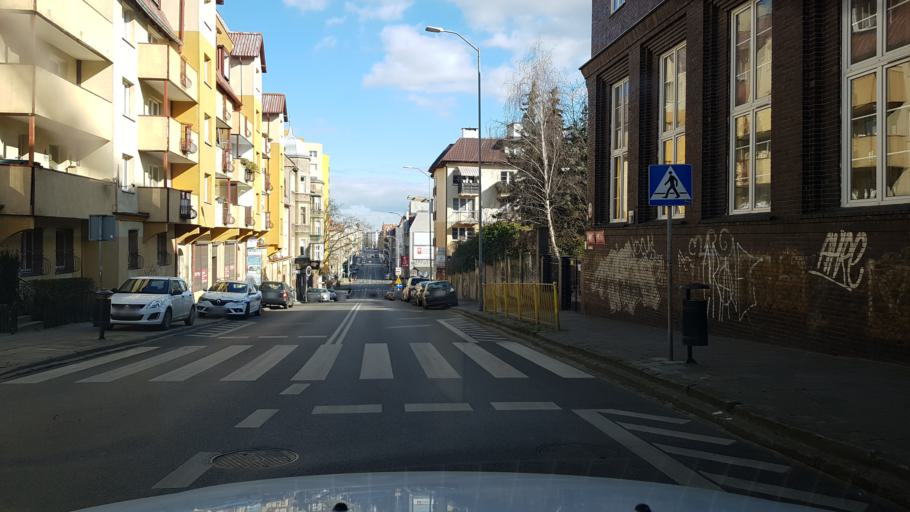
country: PL
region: West Pomeranian Voivodeship
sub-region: Szczecin
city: Szczecin
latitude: 53.4338
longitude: 14.5296
